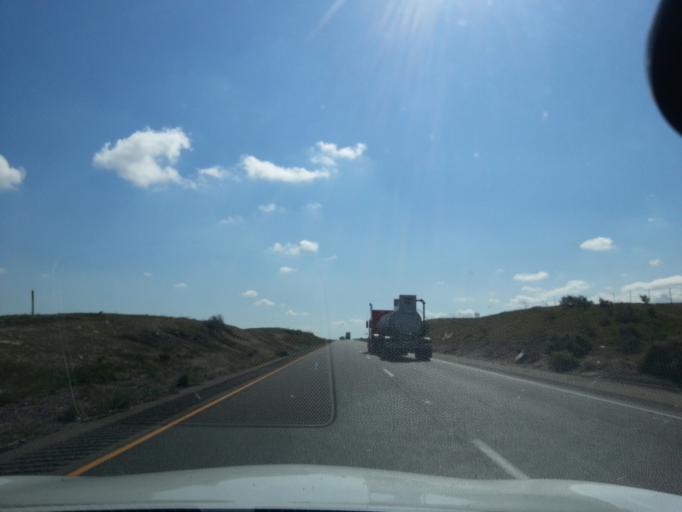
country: US
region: California
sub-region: Fresno County
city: Mendota
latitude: 36.5165
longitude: -120.4705
